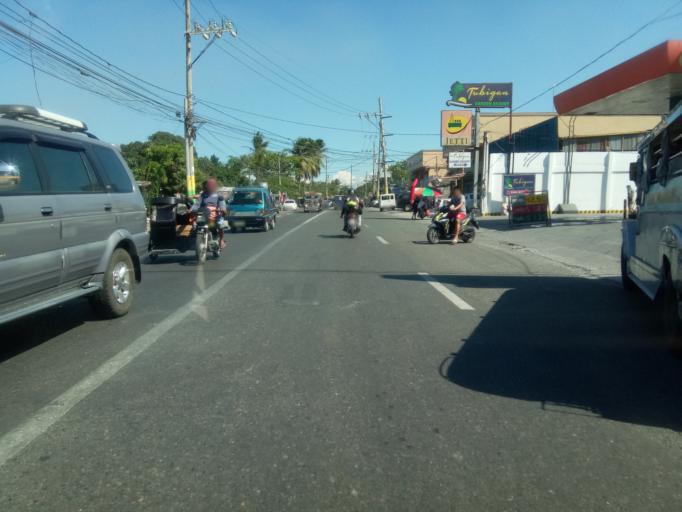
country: PH
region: Calabarzon
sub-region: Province of Cavite
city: Bulihan
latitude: 14.3194
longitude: 120.9854
